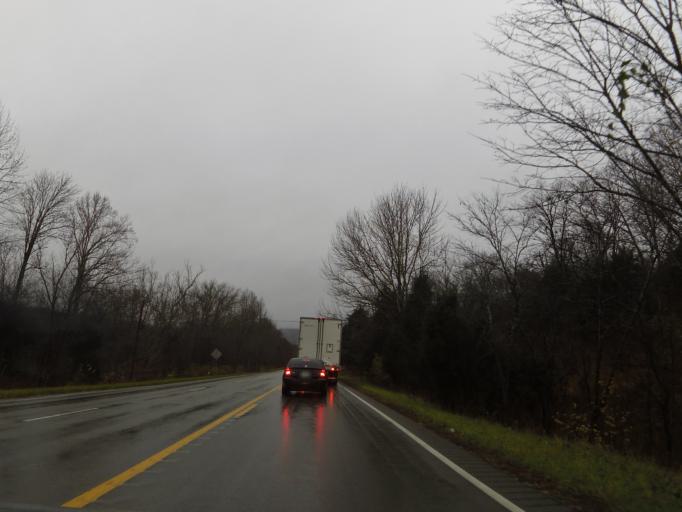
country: US
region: Kentucky
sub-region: Rockcastle County
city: Mount Vernon
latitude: 37.4065
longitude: -84.3360
